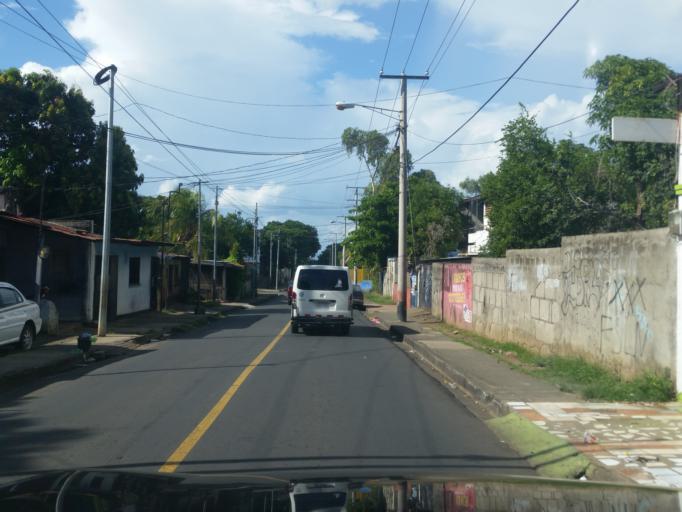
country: NI
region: Managua
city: Managua
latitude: 12.1465
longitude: -86.2683
